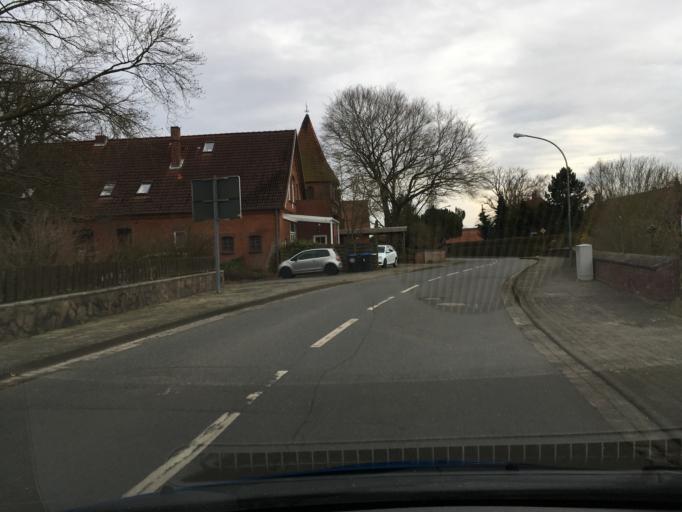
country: DE
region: Lower Saxony
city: Oetzen
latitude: 52.9990
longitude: 10.6511
